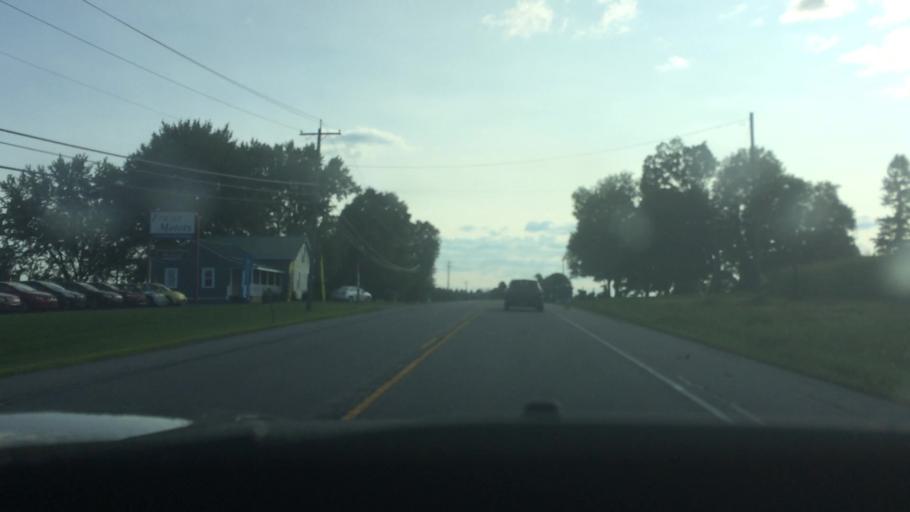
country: US
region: New York
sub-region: St. Lawrence County
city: Canton
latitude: 44.6080
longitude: -75.1255
